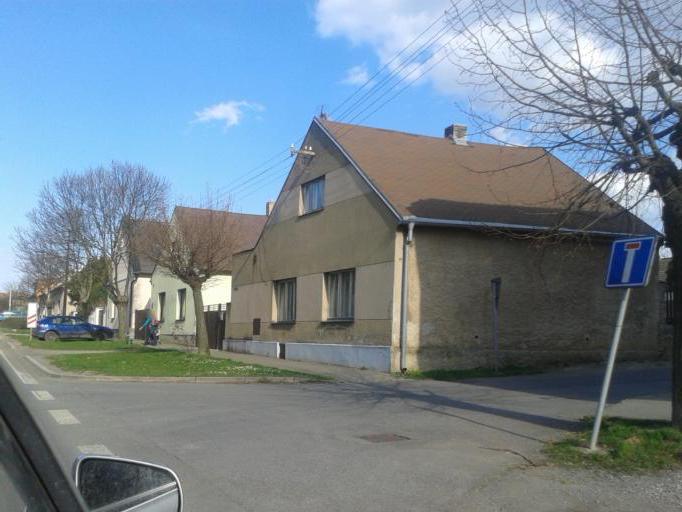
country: CZ
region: Central Bohemia
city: Rudna
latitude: 50.0345
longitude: 14.2333
